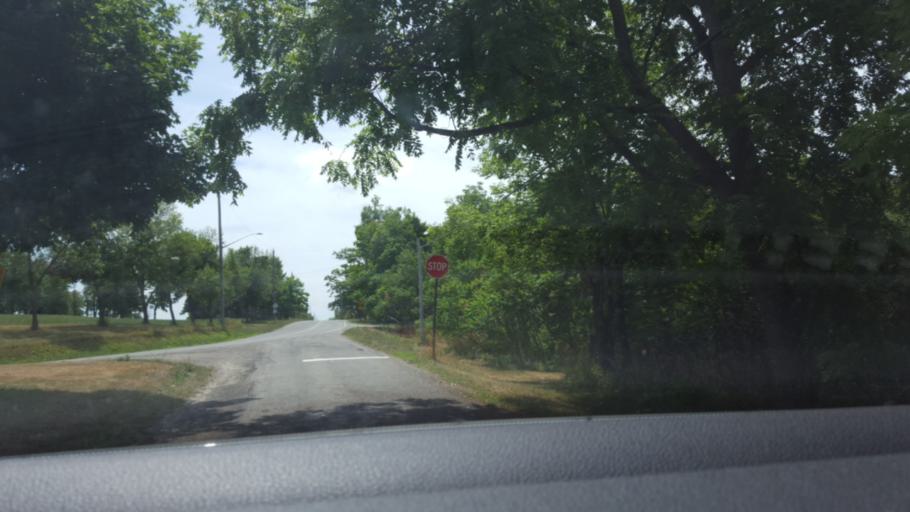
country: CA
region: Ontario
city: Hamilton
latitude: 43.1844
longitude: -79.5711
